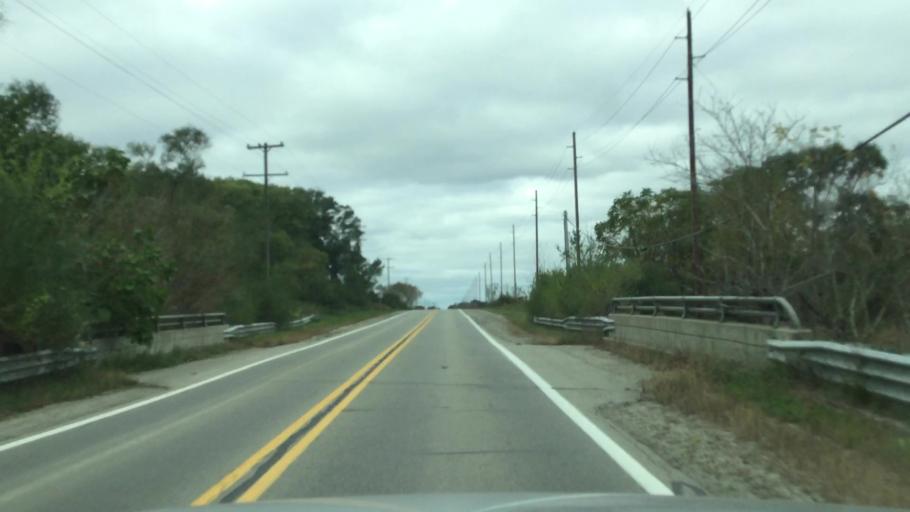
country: US
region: Michigan
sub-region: Macomb County
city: Armada
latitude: 42.8066
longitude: -82.8713
